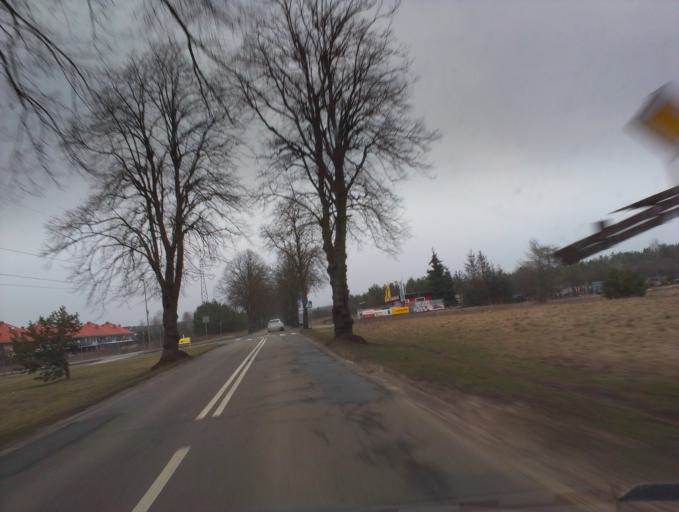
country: PL
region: Greater Poland Voivodeship
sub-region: Powiat pilski
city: Pila
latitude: 53.1802
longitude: 16.7536
